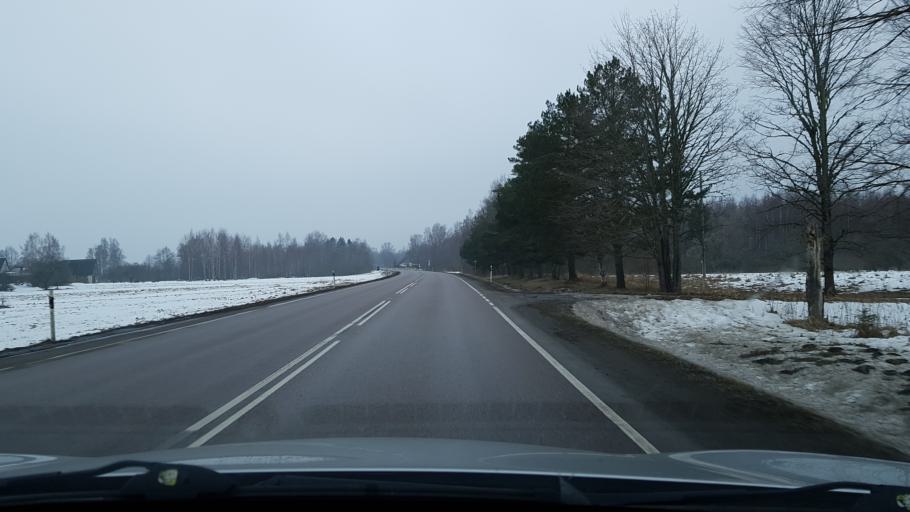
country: EE
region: Jogevamaa
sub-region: Poltsamaa linn
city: Poltsamaa
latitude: 58.4027
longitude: 25.9798
